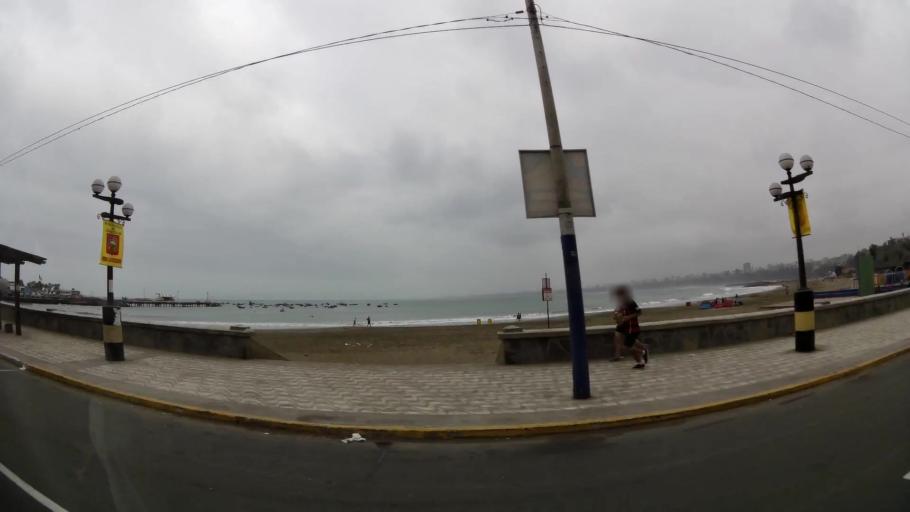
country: PE
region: Lima
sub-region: Lima
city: Surco
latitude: -12.1652
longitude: -77.0273
